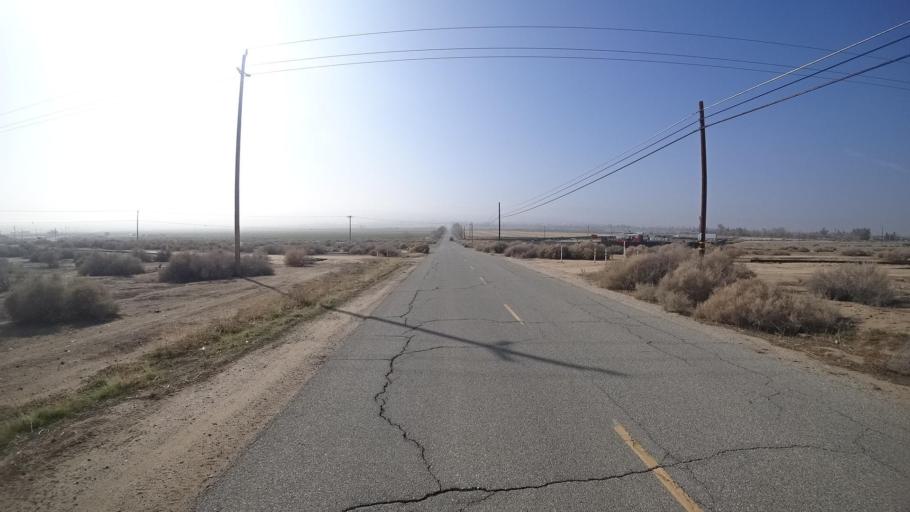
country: US
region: California
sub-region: Kern County
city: Ford City
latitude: 35.1526
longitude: -119.4306
